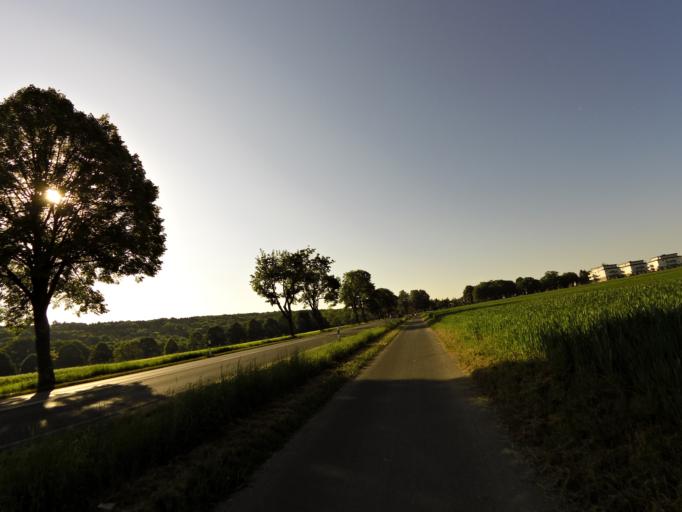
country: DE
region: North Rhine-Westphalia
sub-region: Regierungsbezirk Koln
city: Bonn
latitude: 50.6885
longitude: 7.0744
